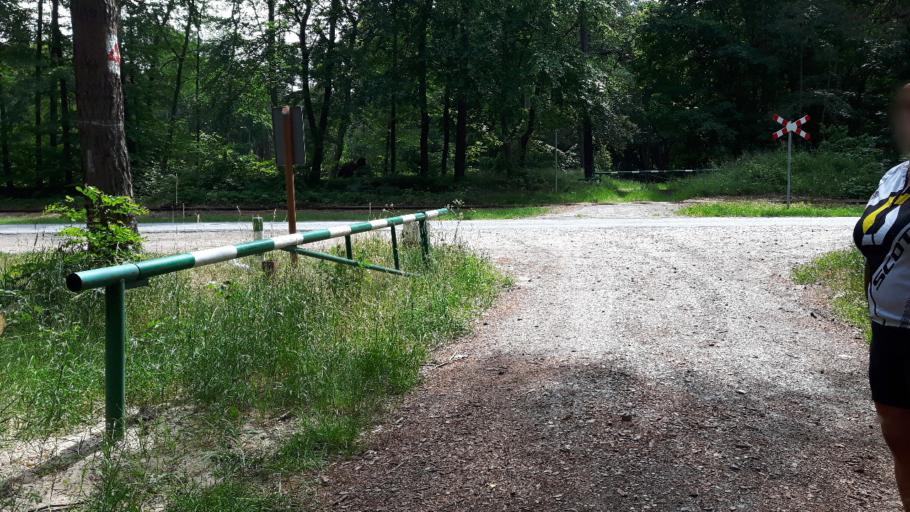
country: PL
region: Pomeranian Voivodeship
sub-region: Powiat nowodworski
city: Stegna
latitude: 54.3345
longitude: 18.9977
